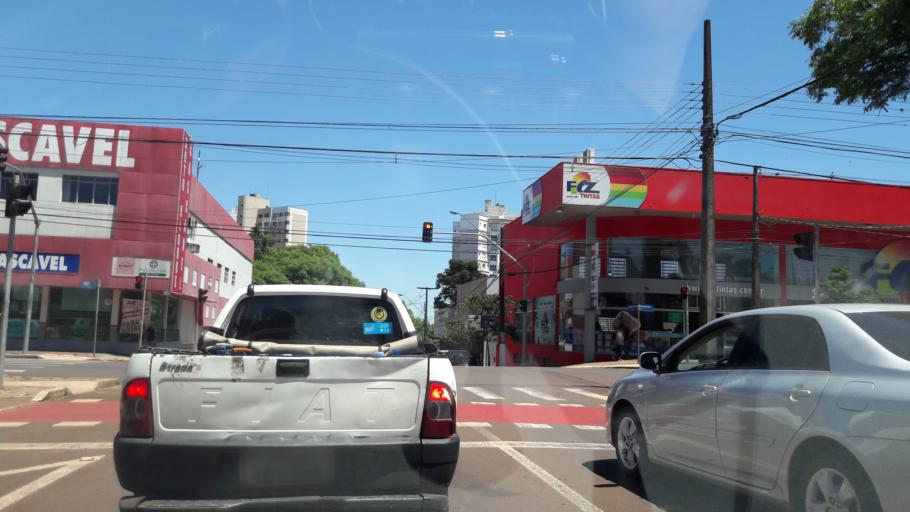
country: BR
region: Parana
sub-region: Cascavel
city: Cascavel
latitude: -24.9499
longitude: -53.4447
